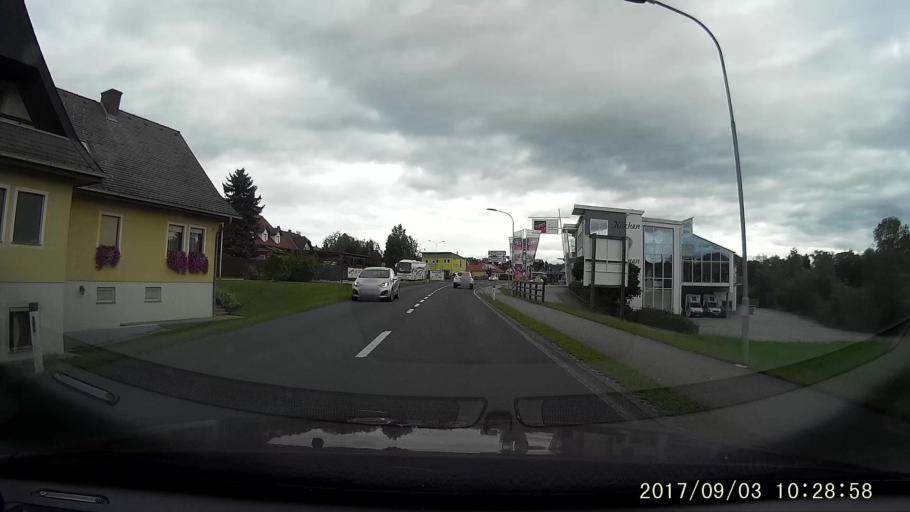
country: AT
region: Styria
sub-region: Politischer Bezirk Hartberg-Fuerstenfeld
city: Ilz
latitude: 47.0865
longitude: 15.9306
